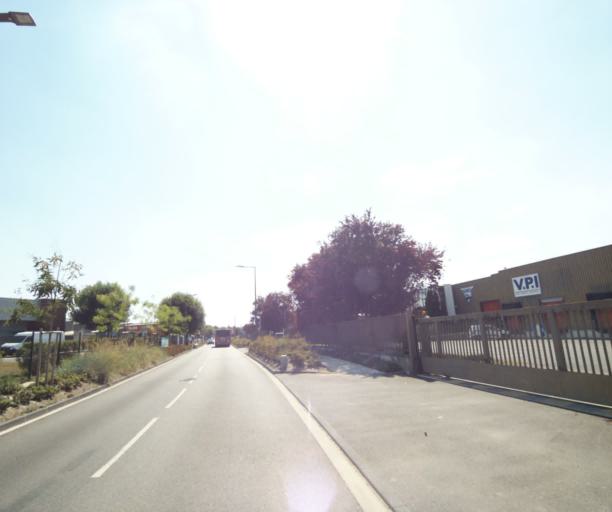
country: FR
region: Ile-de-France
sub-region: Departement de Seine-et-Marne
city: Saint-Thibault-des-Vignes
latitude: 48.8732
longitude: 2.6833
